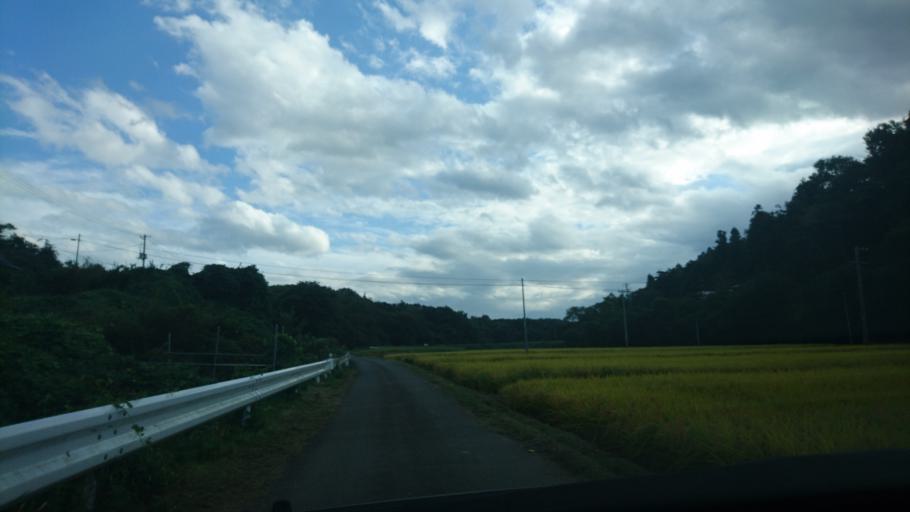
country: JP
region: Iwate
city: Ichinoseki
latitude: 38.8953
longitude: 141.1522
